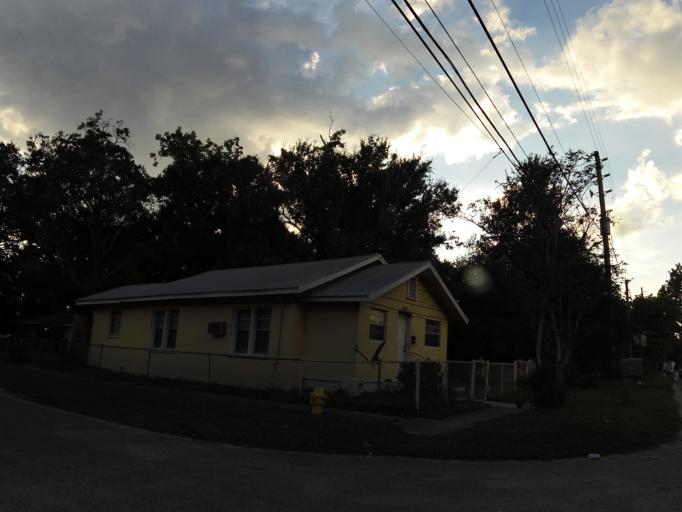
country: US
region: Florida
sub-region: Duval County
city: Jacksonville
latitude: 30.3373
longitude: -81.6929
